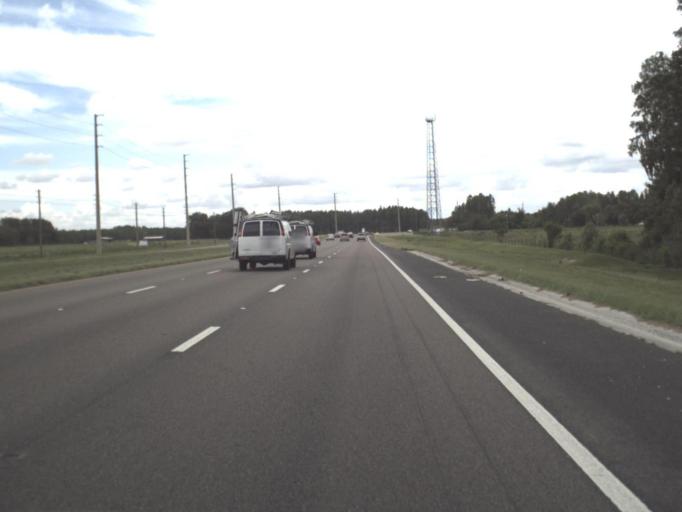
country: US
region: Florida
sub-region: Pasco County
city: Odessa
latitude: 28.1922
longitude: -82.5764
